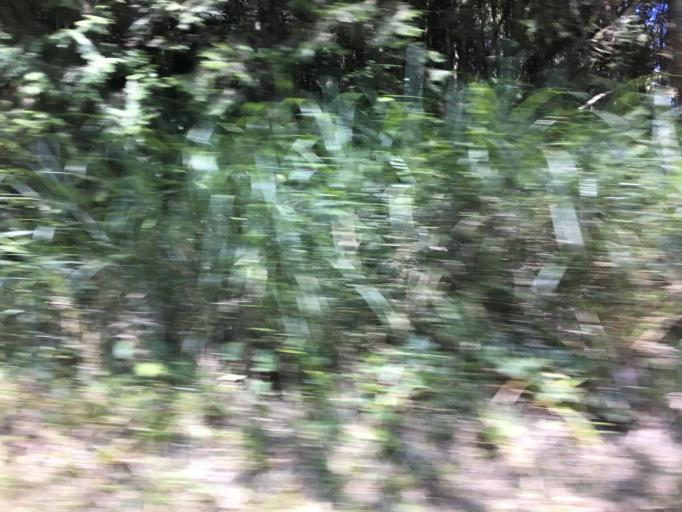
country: TW
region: Taiwan
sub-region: Yilan
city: Yilan
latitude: 24.5182
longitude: 121.5223
